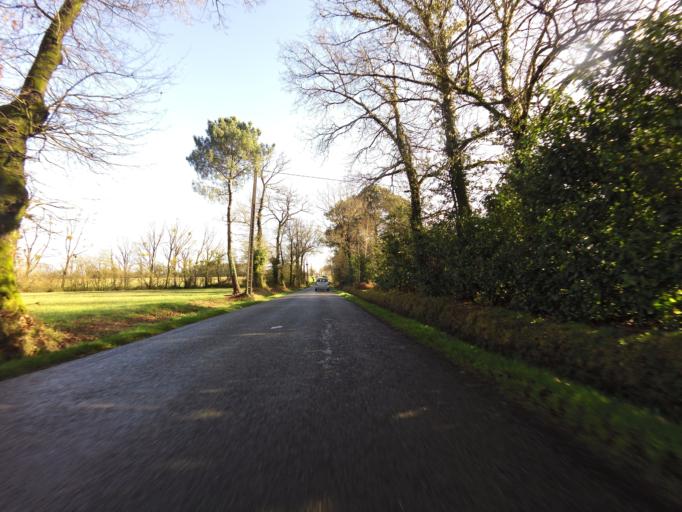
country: FR
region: Brittany
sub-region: Departement du Morbihan
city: Limerzel
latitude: 47.6518
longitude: -2.3857
